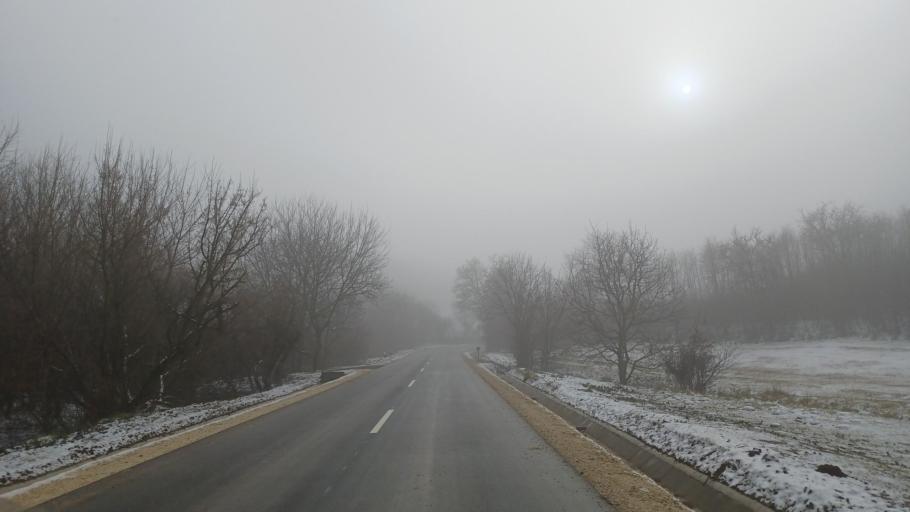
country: HU
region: Tolna
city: Gyonk
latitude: 46.5822
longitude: 18.4748
